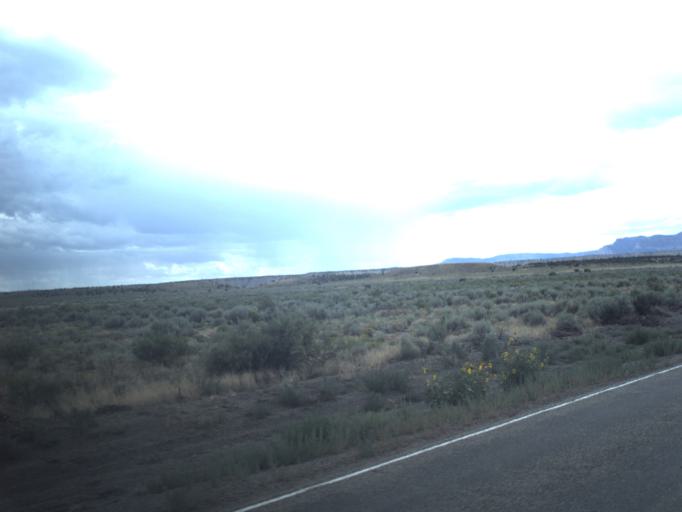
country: US
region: Utah
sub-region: Carbon County
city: Price
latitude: 39.4867
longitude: -110.8768
